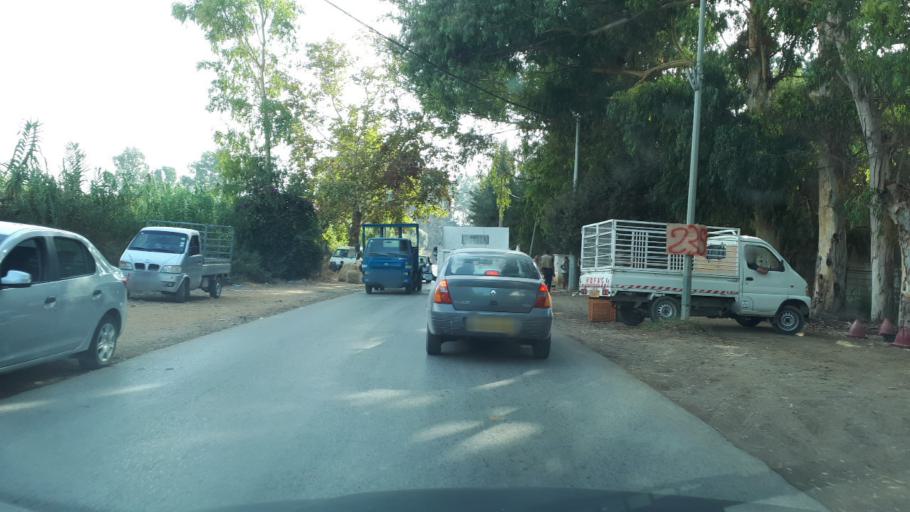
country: DZ
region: Tipaza
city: Zeralda
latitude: 36.7295
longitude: 2.8953
